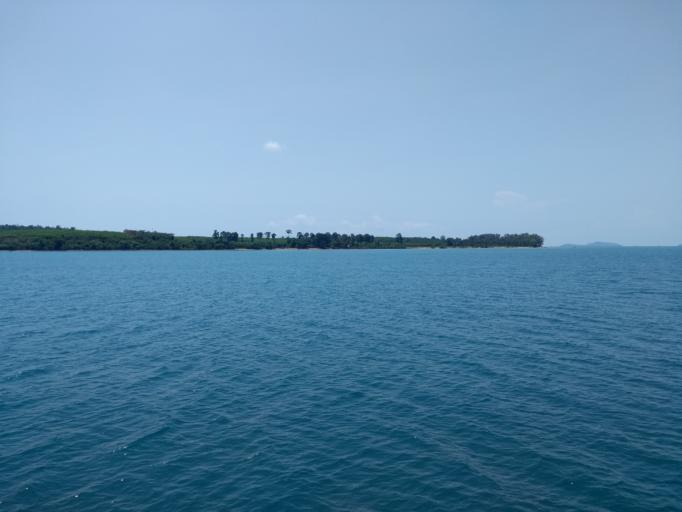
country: TH
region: Trat
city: Ko Kut
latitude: 11.8112
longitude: 102.5147
